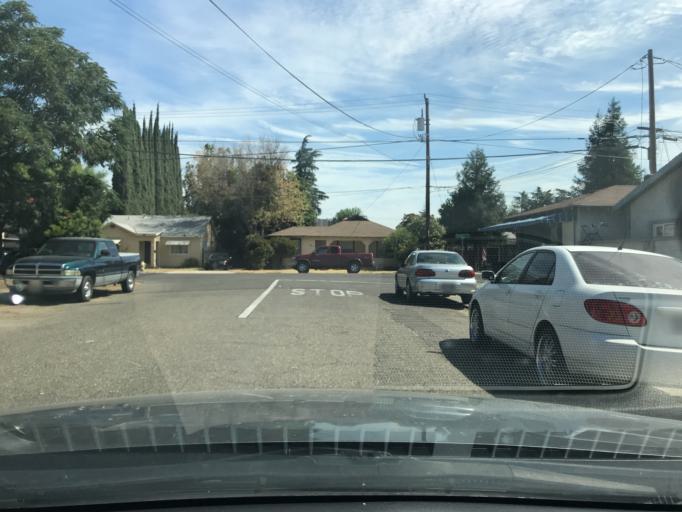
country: US
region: California
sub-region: Merced County
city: Atwater
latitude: 37.3483
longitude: -120.6093
